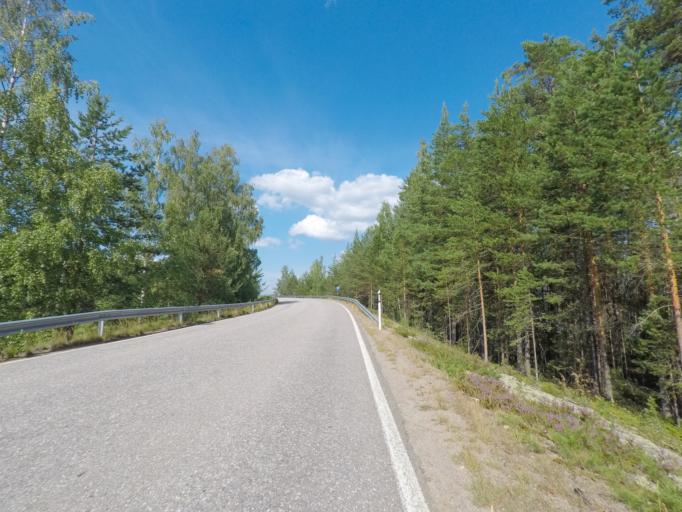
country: FI
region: Southern Savonia
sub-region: Mikkeli
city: Puumala
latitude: 61.4674
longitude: 28.1690
